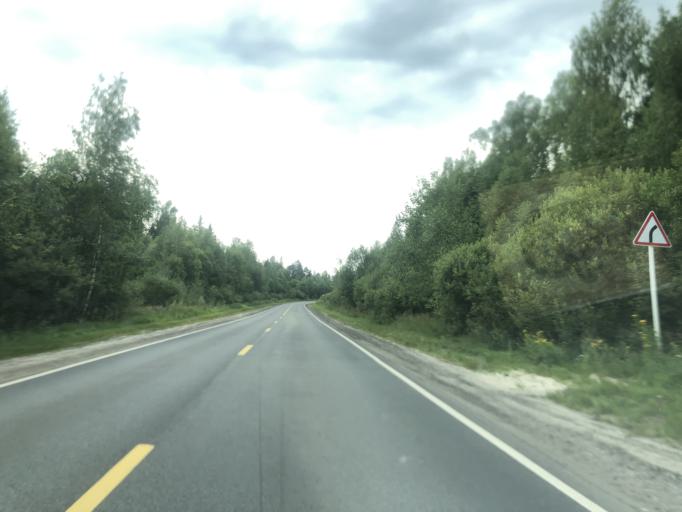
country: RU
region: Ivanovo
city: Verkhniy Landekh
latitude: 56.7652
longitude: 42.4578
